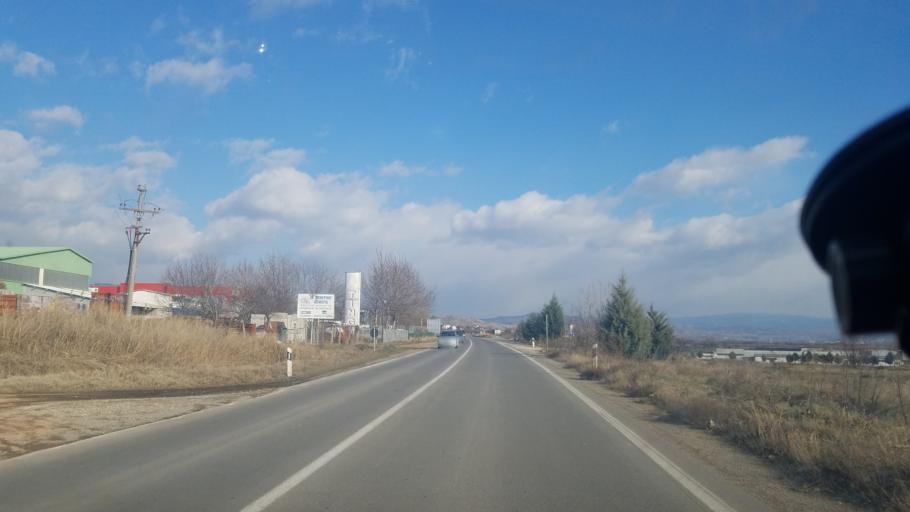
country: MK
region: Kocani
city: Kochani
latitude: 41.9006
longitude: 22.3845
